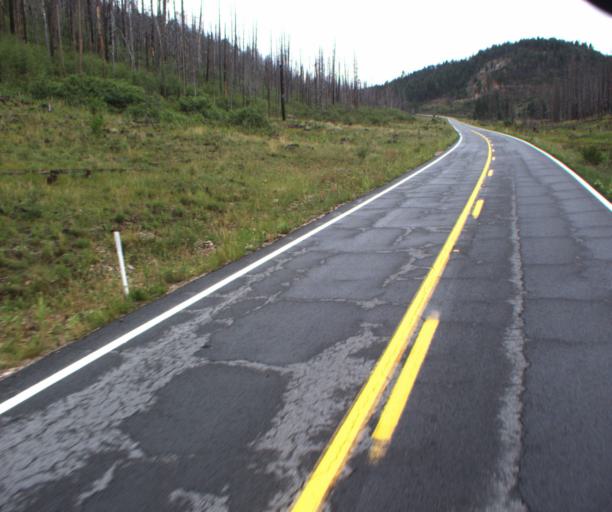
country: US
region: Arizona
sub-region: Apache County
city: Eagar
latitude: 33.7968
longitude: -109.1546
